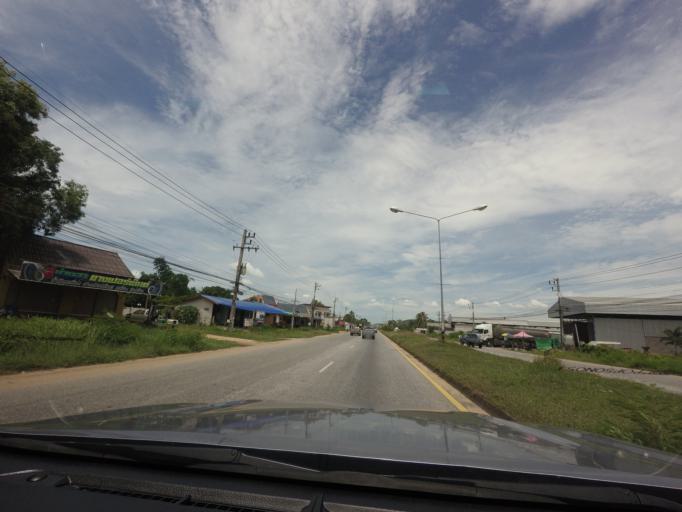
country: TH
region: Songkhla
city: Singhanakhon
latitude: 7.2440
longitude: 100.5428
